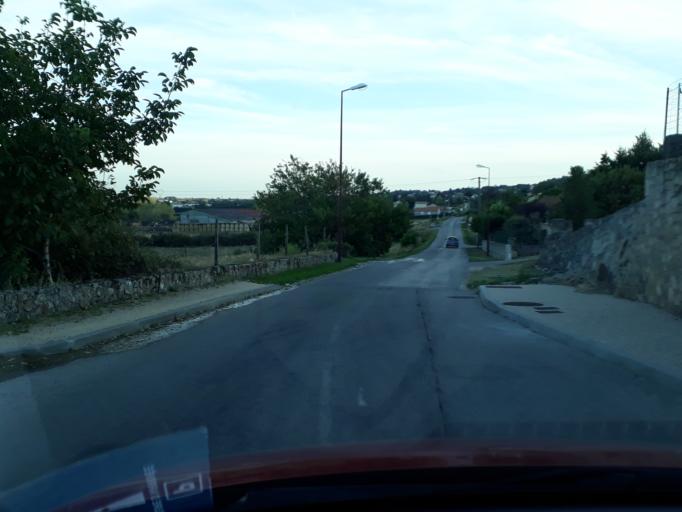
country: FR
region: Rhone-Alpes
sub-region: Departement de l'Ardeche
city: Felines
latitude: 45.3151
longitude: 4.7283
